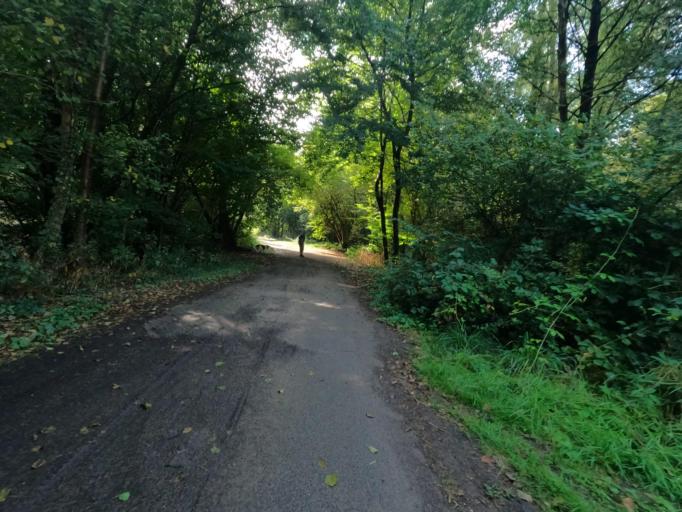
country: DE
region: North Rhine-Westphalia
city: Huckelhoven
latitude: 51.0898
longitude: 6.2077
